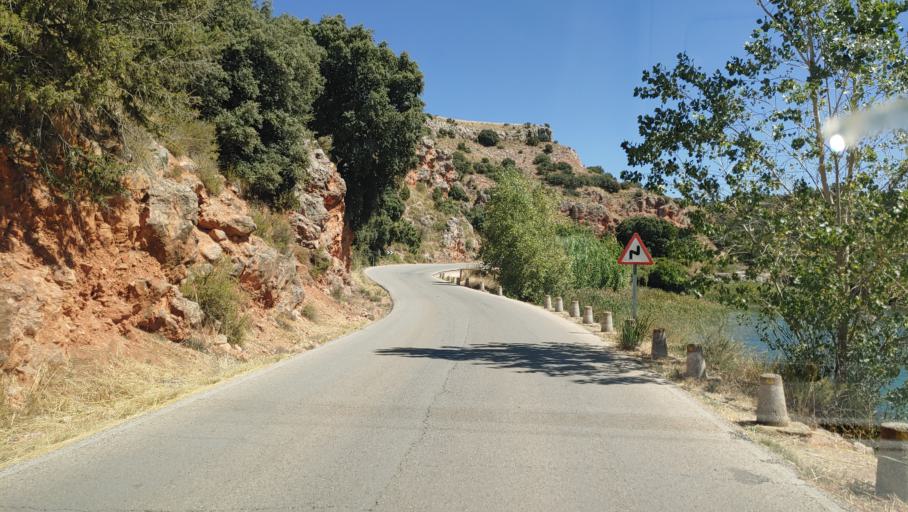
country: ES
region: Castille-La Mancha
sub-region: Provincia de Ciudad Real
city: Ruidera
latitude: 38.9409
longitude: -2.8515
